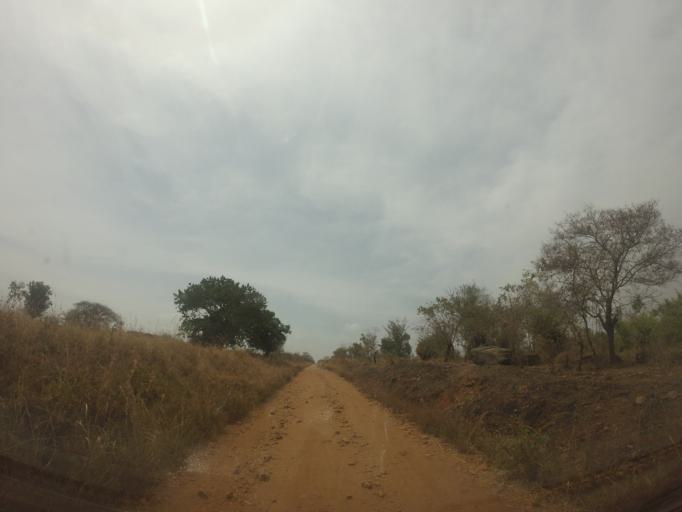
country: UG
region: Northern Region
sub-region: Nebbi District
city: Nebbi
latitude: 2.6322
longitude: 31.0349
